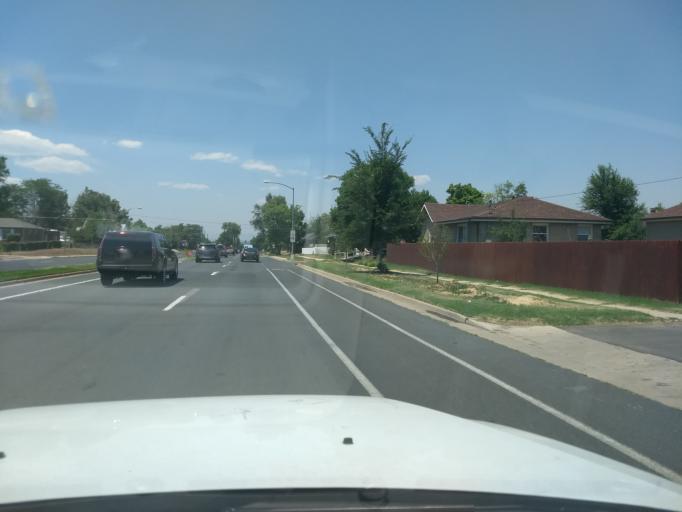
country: US
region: Colorado
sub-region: Denver County
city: Denver
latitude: 39.7620
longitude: -104.9530
